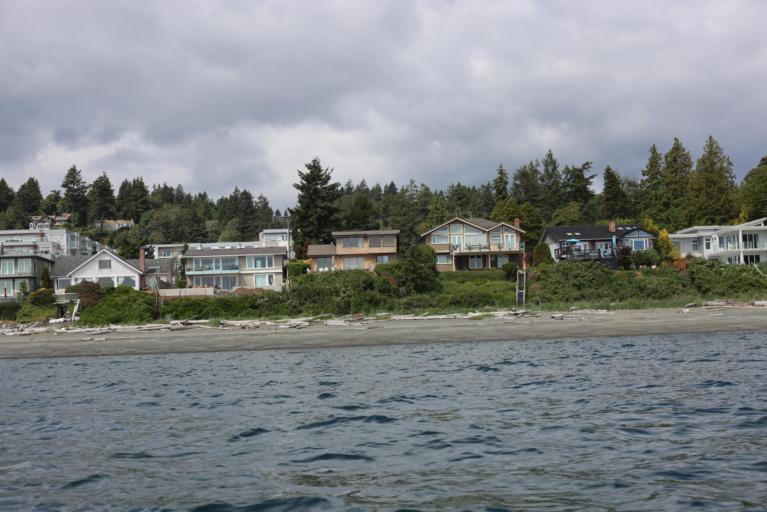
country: CA
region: British Columbia
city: Victoria
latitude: 48.5228
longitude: -123.3645
